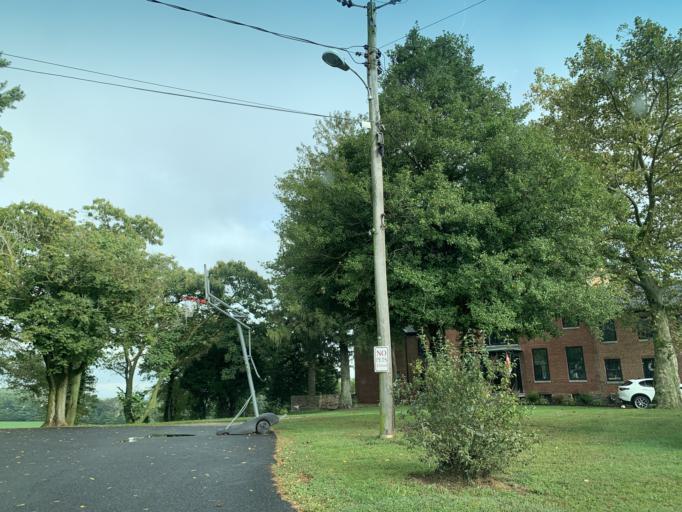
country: US
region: Maryland
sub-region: Harford County
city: Havre de Grace
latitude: 39.5621
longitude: -76.1282
